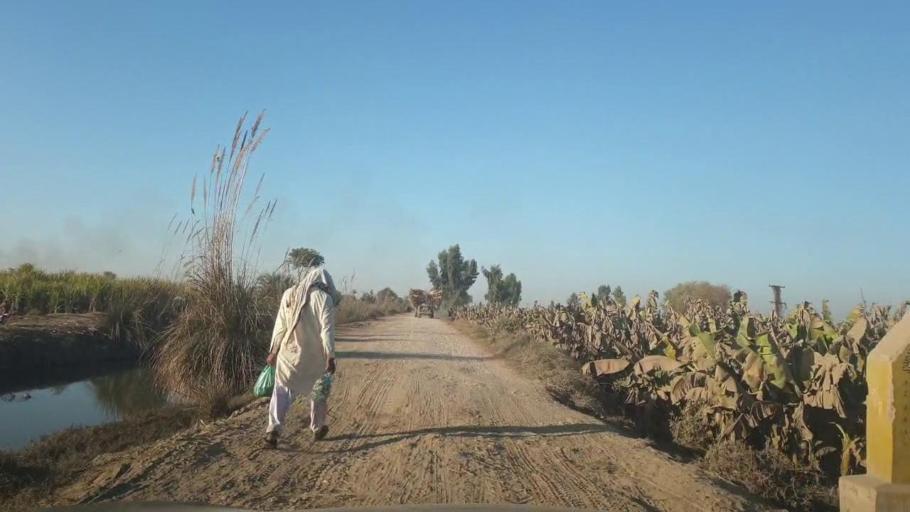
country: PK
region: Sindh
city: Ghotki
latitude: 27.9963
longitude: 69.2717
